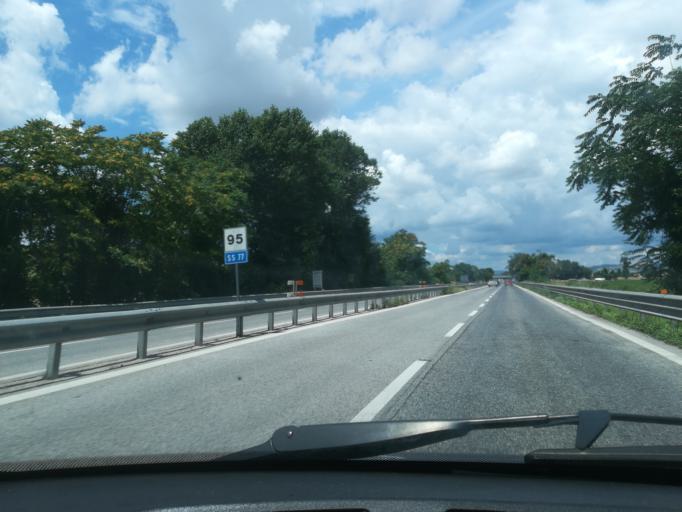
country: IT
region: The Marches
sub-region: Provincia di Macerata
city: Villa San Filippo
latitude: 43.2638
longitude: 13.5545
